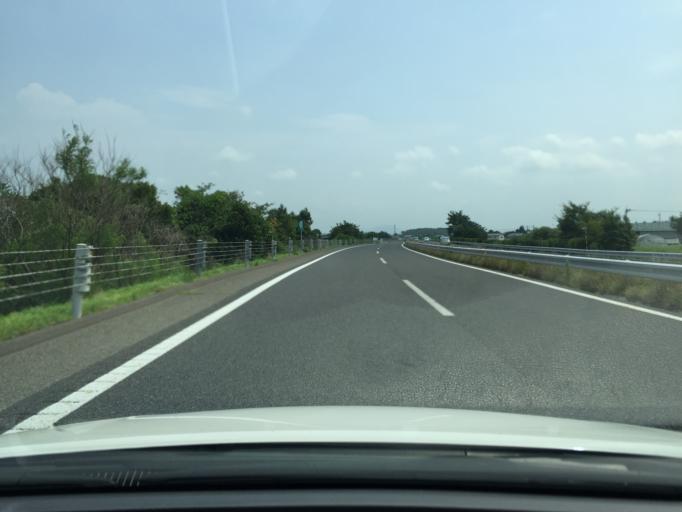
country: JP
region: Fukushima
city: Koriyama
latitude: 37.4554
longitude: 140.3990
